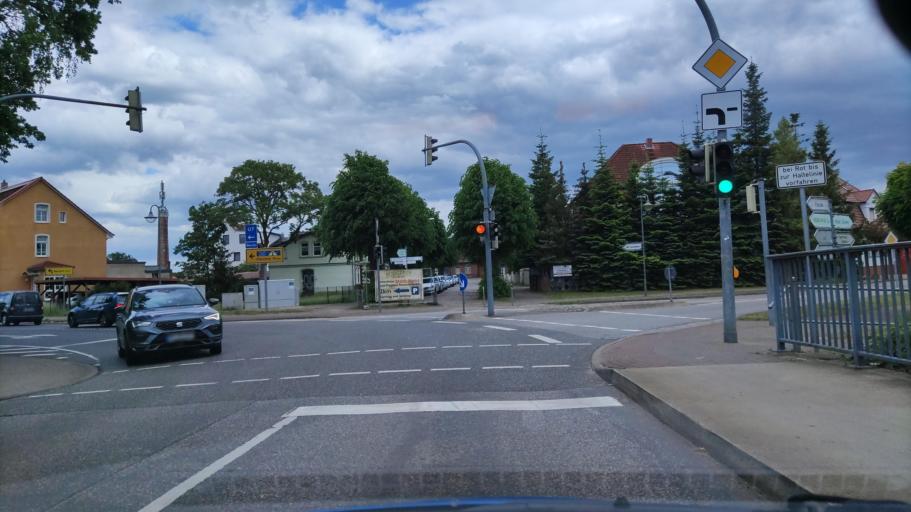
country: DE
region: Mecklenburg-Vorpommern
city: Neustadt-Glewe
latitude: 53.3787
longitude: 11.5920
